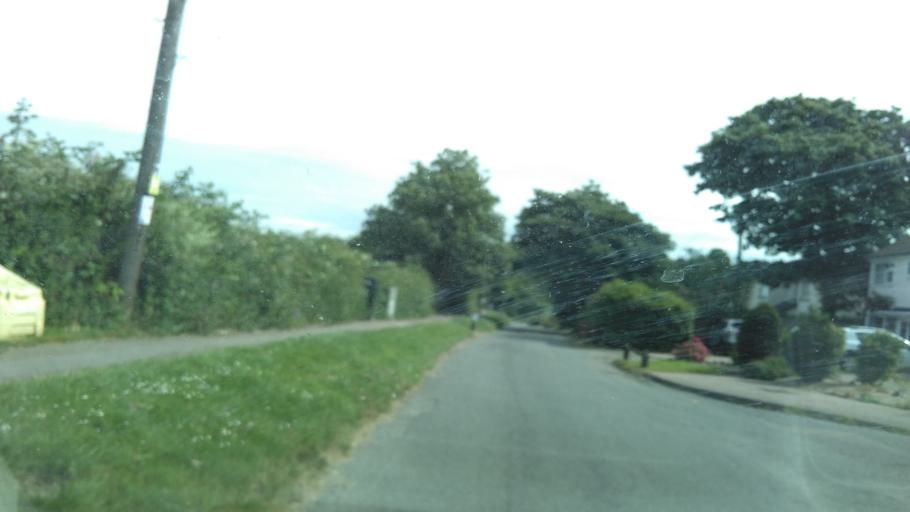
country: GB
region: England
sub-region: Kent
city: Canterbury
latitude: 51.2593
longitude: 1.0652
